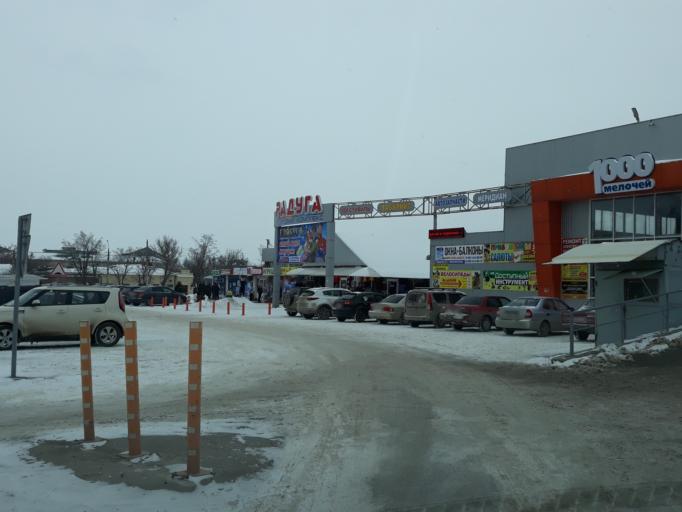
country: RU
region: Rostov
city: Taganrog
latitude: 47.2198
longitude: 38.9161
